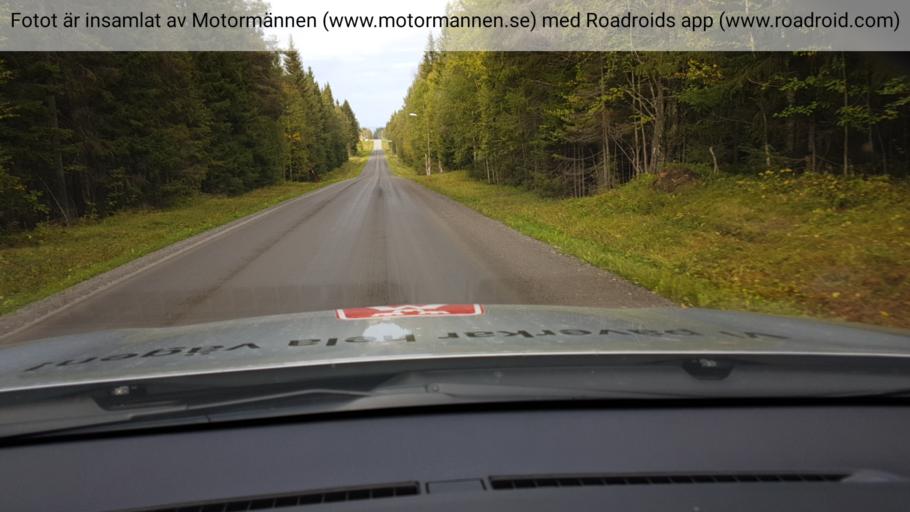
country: SE
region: Jaemtland
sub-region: Stroemsunds Kommun
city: Stroemsund
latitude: 64.0600
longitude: 15.8162
